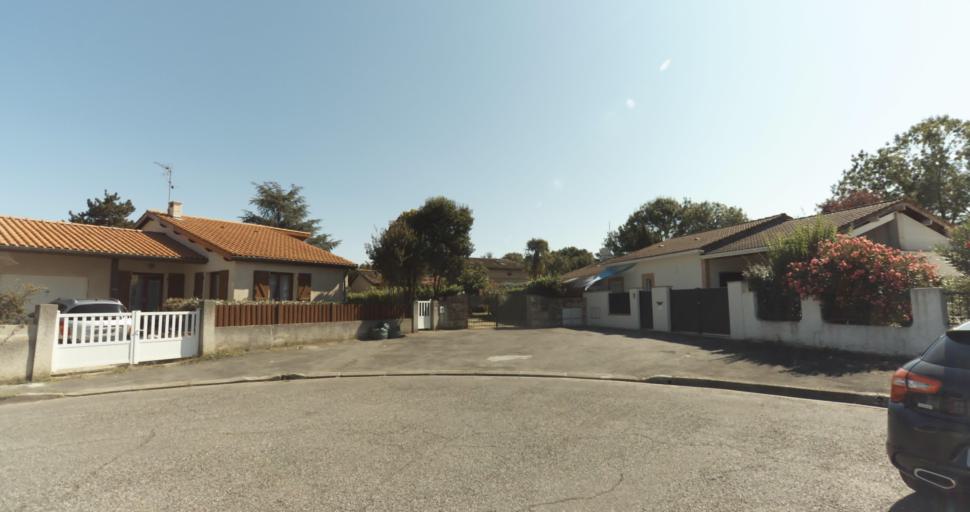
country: FR
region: Midi-Pyrenees
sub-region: Departement de la Haute-Garonne
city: L'Union
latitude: 43.6446
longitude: 1.4790
